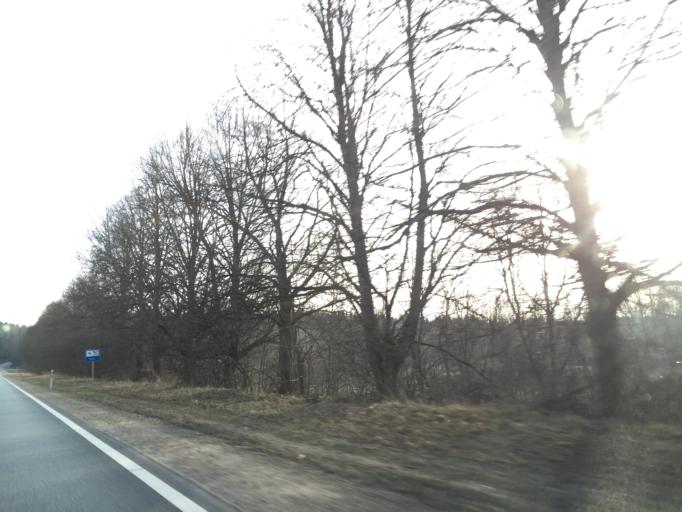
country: LV
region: Seja
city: Loja
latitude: 57.1293
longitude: 24.6610
